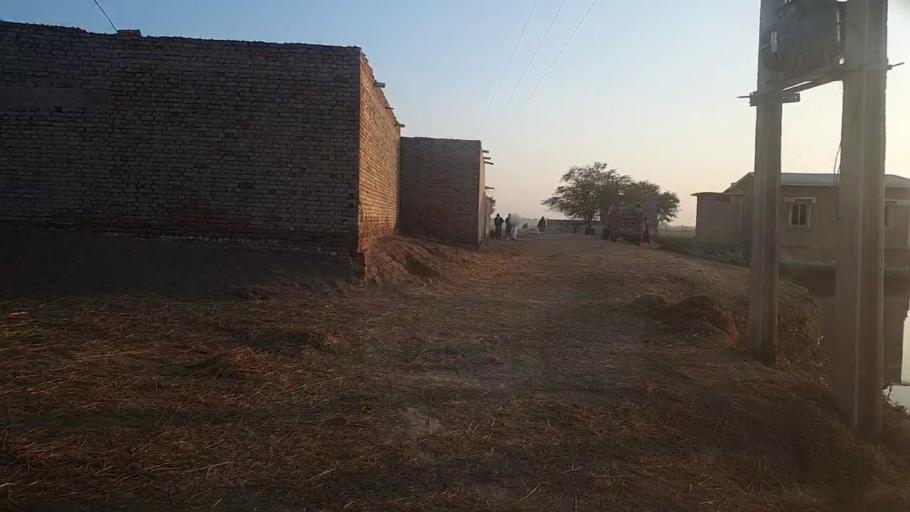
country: PK
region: Sindh
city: Khairpur Nathan Shah
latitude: 27.1698
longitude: 67.7327
